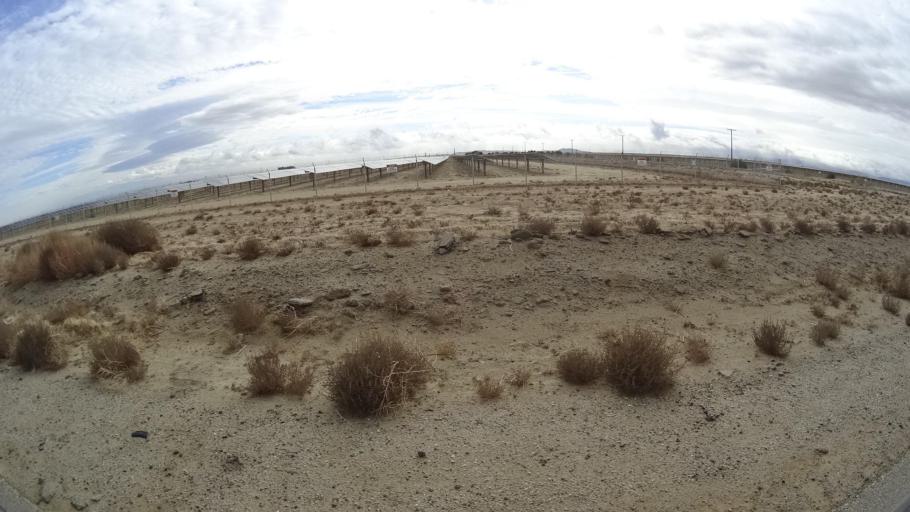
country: US
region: California
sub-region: Kern County
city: Rosamond
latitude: 34.8630
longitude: -118.3701
